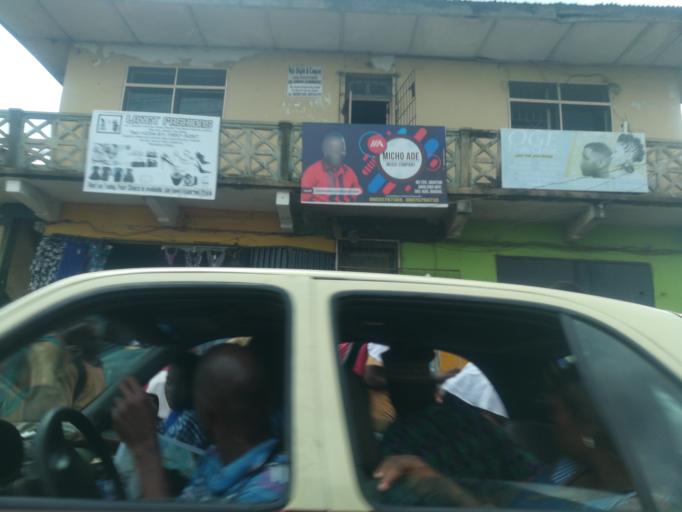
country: NG
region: Oyo
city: Ibadan
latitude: 7.3663
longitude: 3.8841
